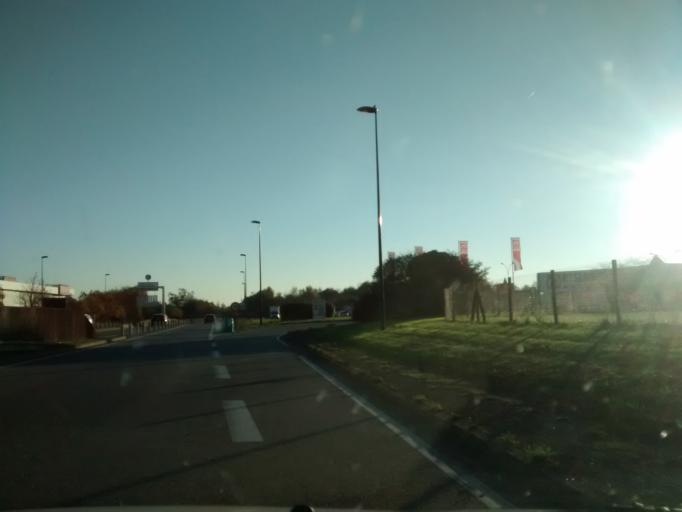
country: FR
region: Brittany
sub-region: Departement d'Ille-et-Vilaine
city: Pace
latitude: 48.1410
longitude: -1.7695
